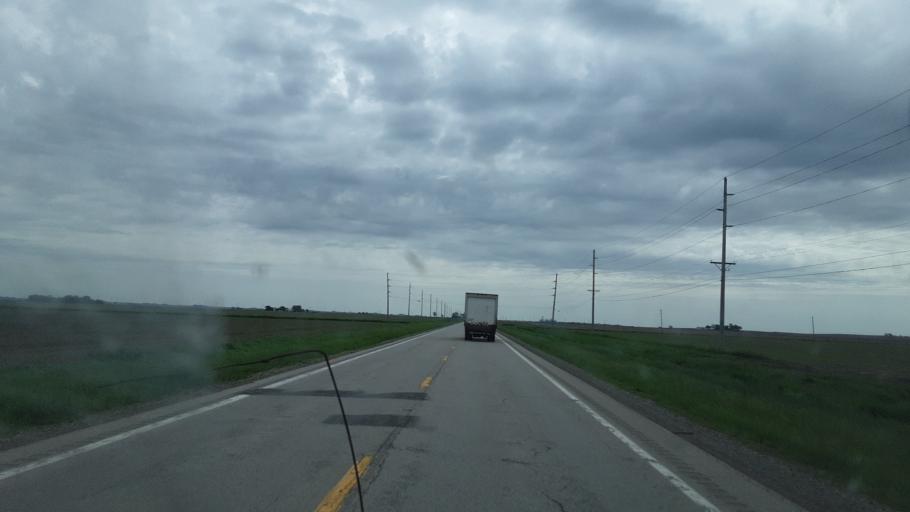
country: US
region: Illinois
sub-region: Tazewell County
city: Delavan
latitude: 40.3060
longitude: -89.5677
